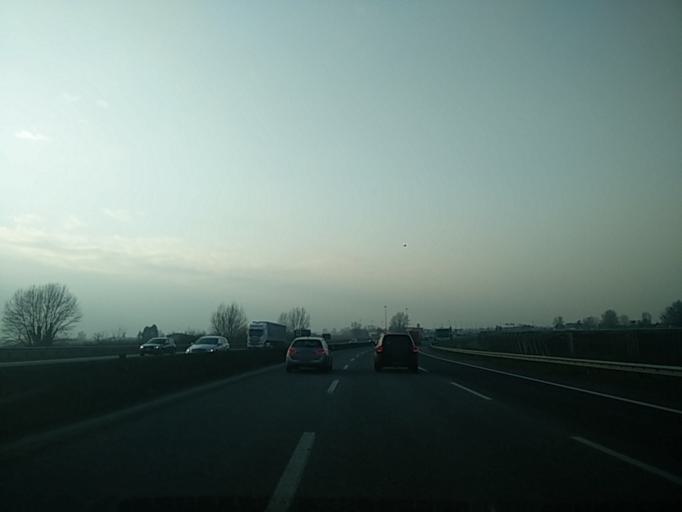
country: IT
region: Emilia-Romagna
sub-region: Provincia di Ravenna
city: Solarolo
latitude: 44.3402
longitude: 11.8538
